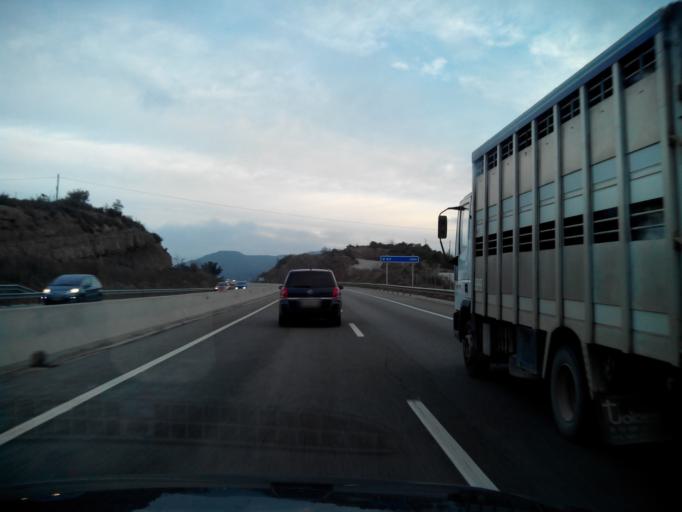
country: ES
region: Catalonia
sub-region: Provincia de Barcelona
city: Puig-reig
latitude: 41.9545
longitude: 1.8844
